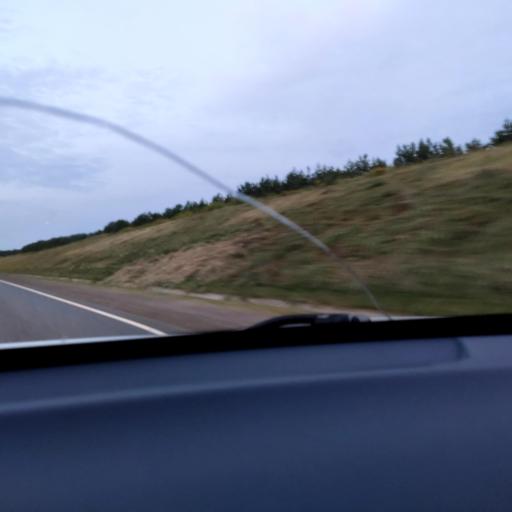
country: RU
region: Tatarstan
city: Verkhniy Uslon
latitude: 55.7163
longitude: 48.8528
